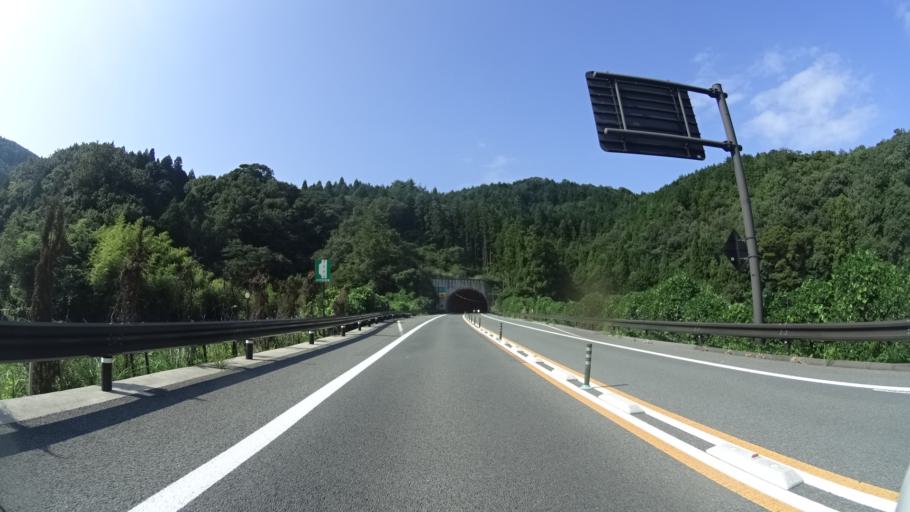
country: JP
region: Shimane
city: Odacho-oda
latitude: 35.0949
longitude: 132.3727
